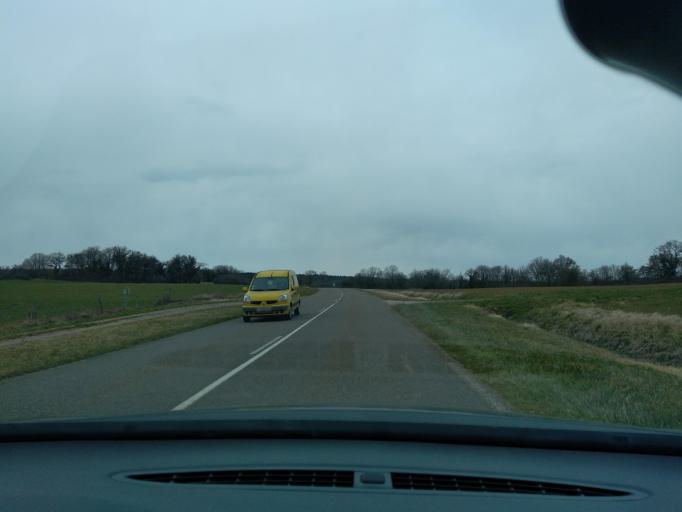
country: FR
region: Franche-Comte
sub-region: Departement du Jura
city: Arinthod
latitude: 46.4455
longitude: 5.5592
